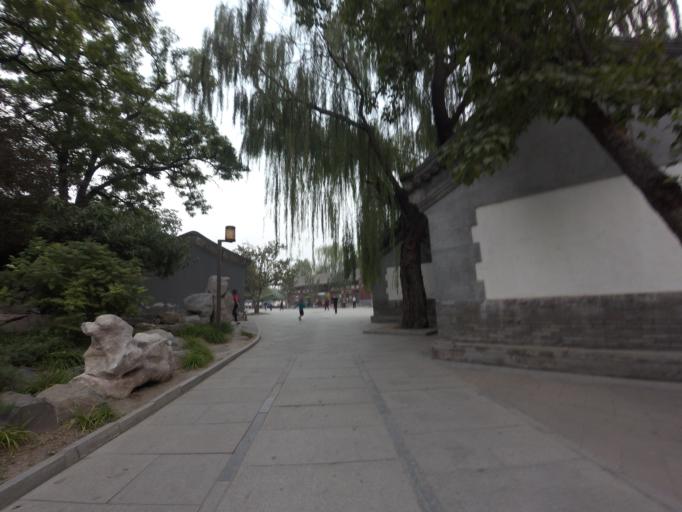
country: CN
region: Beijing
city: Beijing
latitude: 39.9232
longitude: 116.3820
